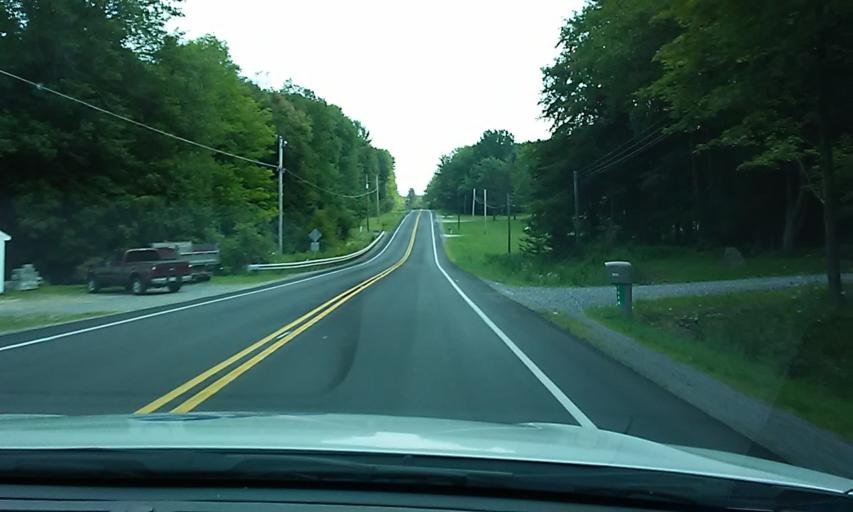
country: US
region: Pennsylvania
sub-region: Elk County
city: Saint Marys
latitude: 41.4446
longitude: -78.4955
